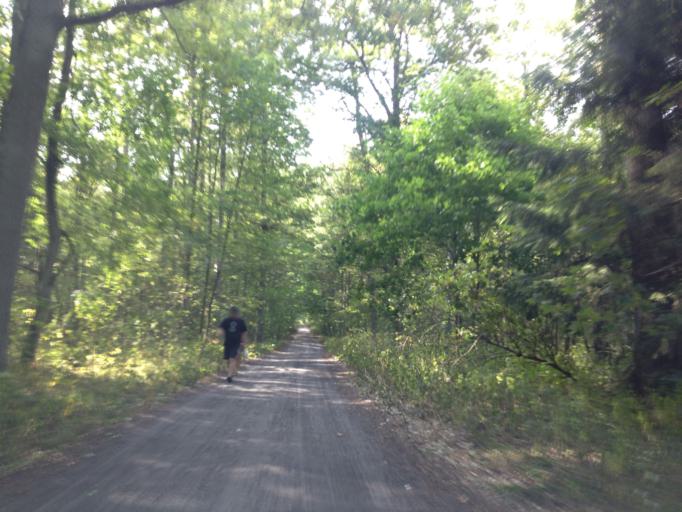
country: PL
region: Kujawsko-Pomorskie
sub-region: Powiat swiecki
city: Swiekatowo
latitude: 53.4973
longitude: 18.1194
